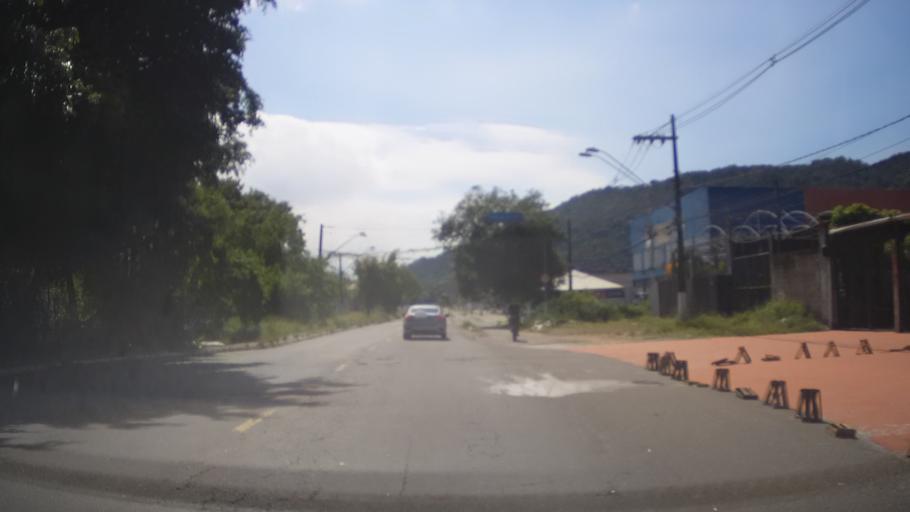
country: BR
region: Sao Paulo
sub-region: Praia Grande
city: Praia Grande
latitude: -23.9876
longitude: -46.3984
